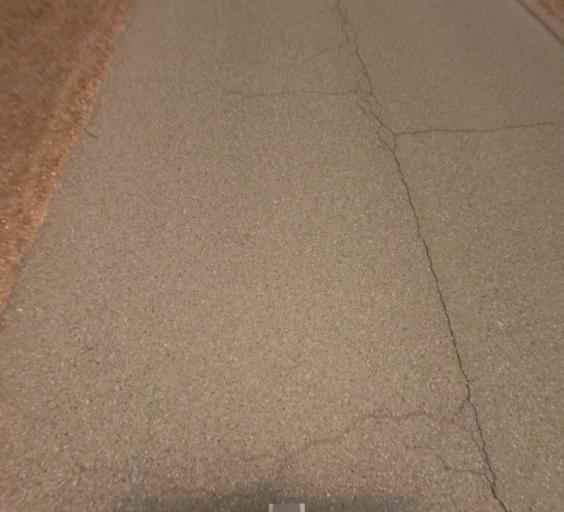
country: US
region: California
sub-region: Madera County
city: Coarsegold
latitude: 37.1952
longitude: -119.6791
